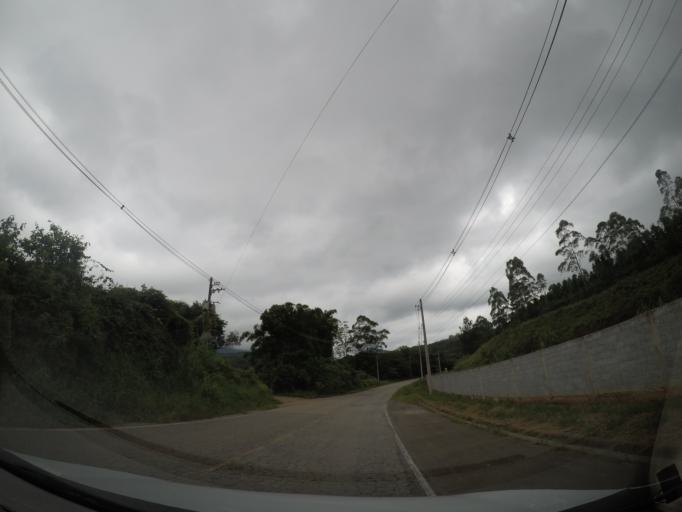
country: BR
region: Sao Paulo
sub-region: Aruja
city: Aruja
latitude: -23.3411
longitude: -46.4044
